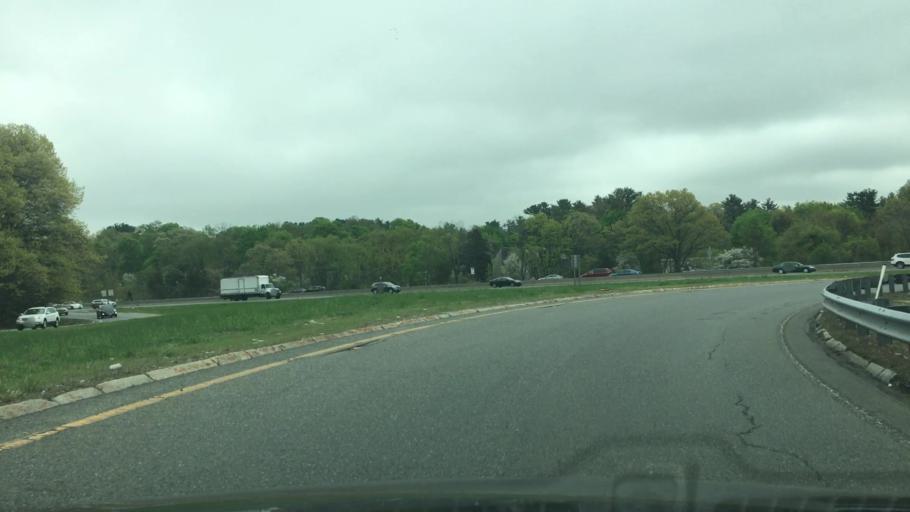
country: US
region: Massachusetts
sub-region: Essex County
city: Lynnfield
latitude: 42.5151
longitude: -71.0269
